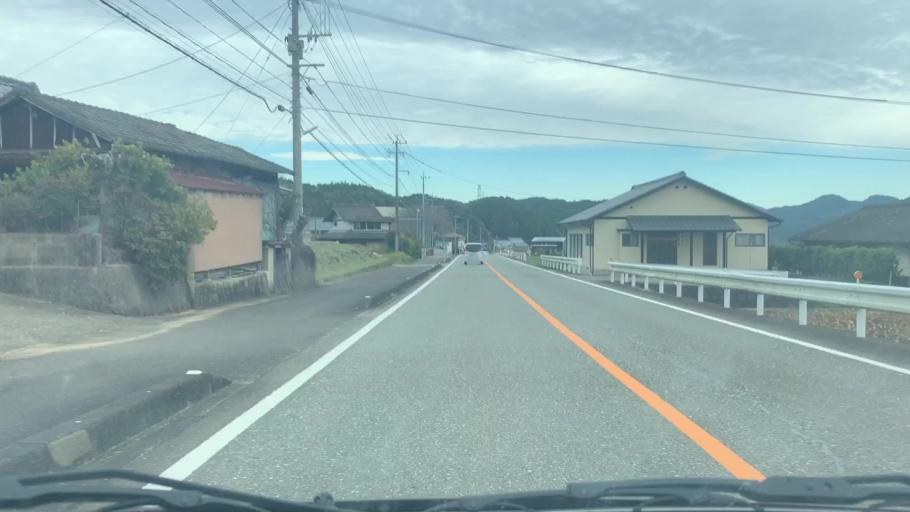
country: JP
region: Saga Prefecture
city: Takeocho-takeo
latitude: 33.1720
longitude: 129.9695
